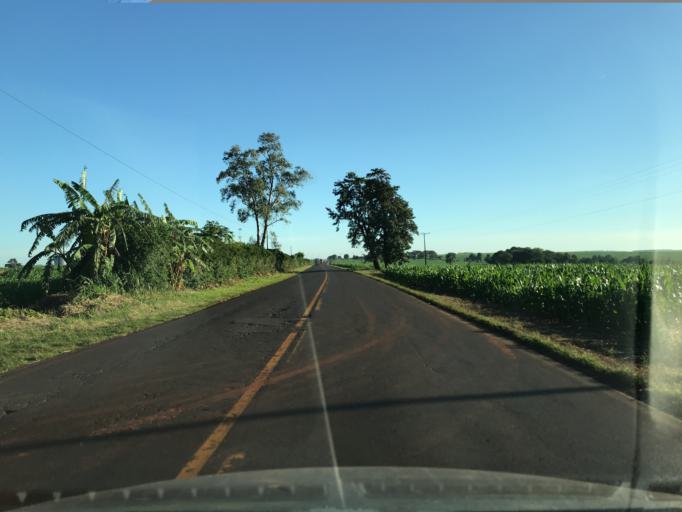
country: BR
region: Parana
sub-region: Palotina
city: Palotina
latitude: -24.1249
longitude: -53.8501
